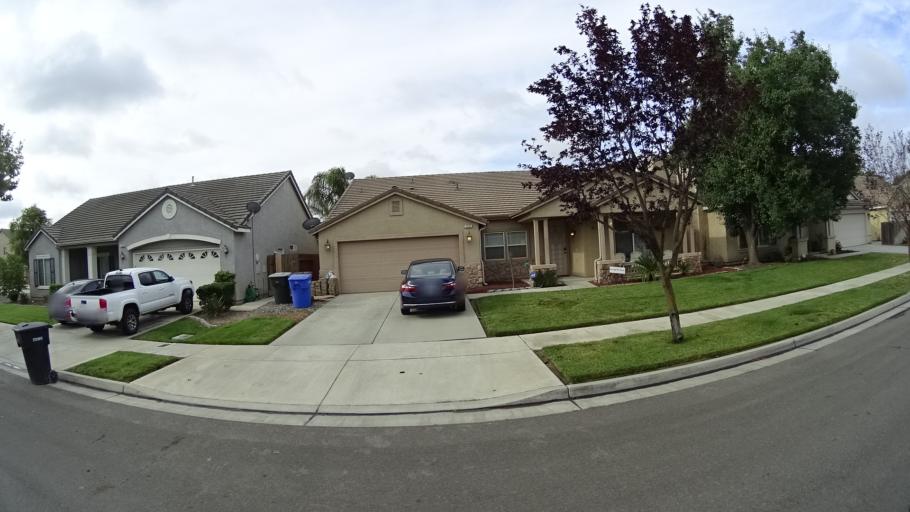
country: US
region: California
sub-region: Kings County
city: Hanford
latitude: 36.3341
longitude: -119.6741
